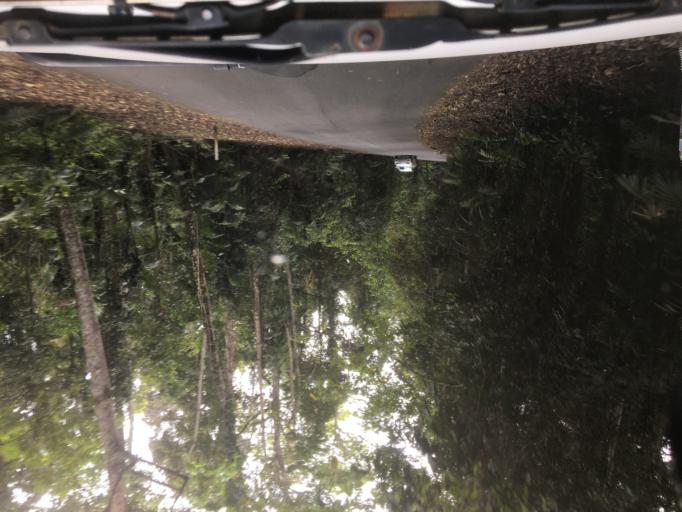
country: AU
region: Queensland
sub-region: Tablelands
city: Tolga
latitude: -17.2798
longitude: 145.6277
